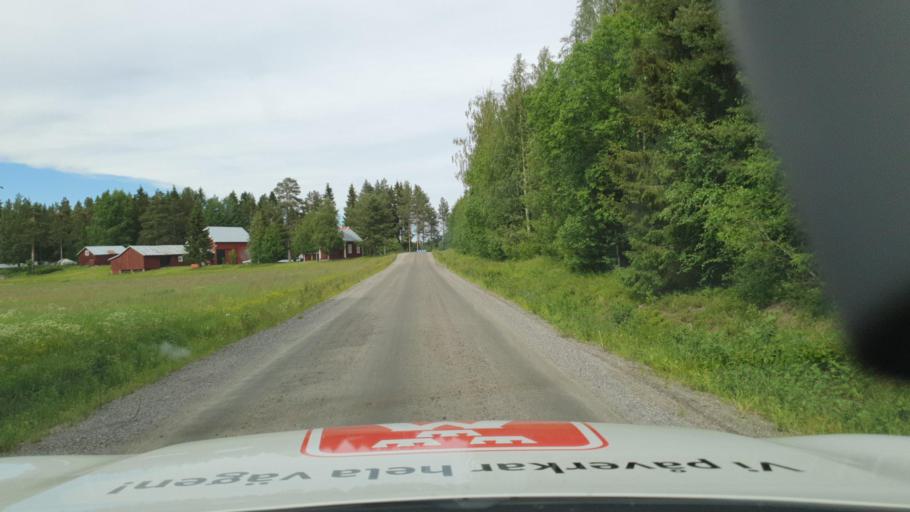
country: SE
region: Vaesterbotten
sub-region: Skelleftea Kommun
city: Viken
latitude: 64.5070
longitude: 20.9297
